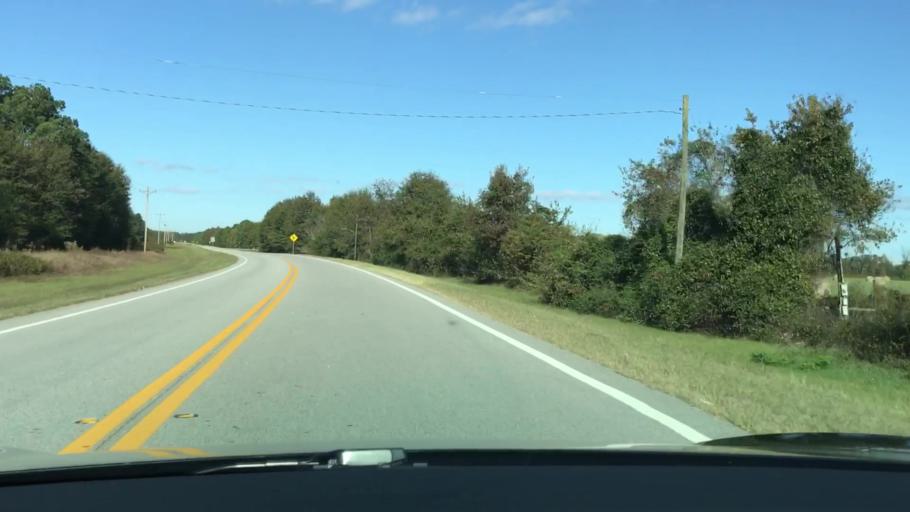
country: US
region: Georgia
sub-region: Glascock County
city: Gibson
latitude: 33.2955
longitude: -82.5130
